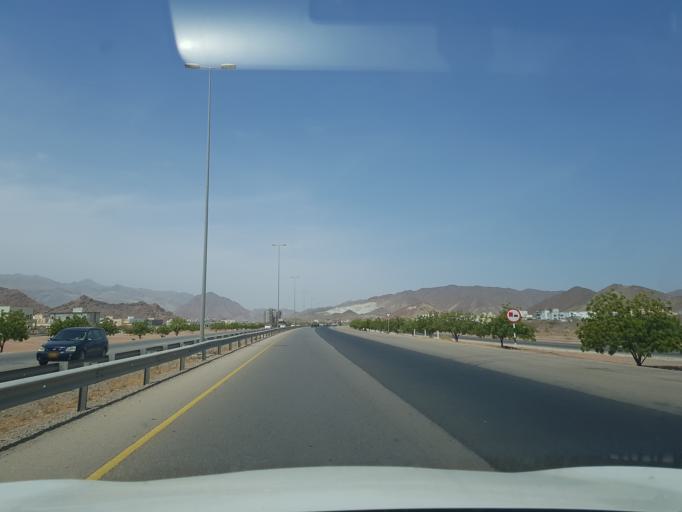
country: OM
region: Muhafazat ad Dakhiliyah
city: Bidbid
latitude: 23.4640
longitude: 58.1535
